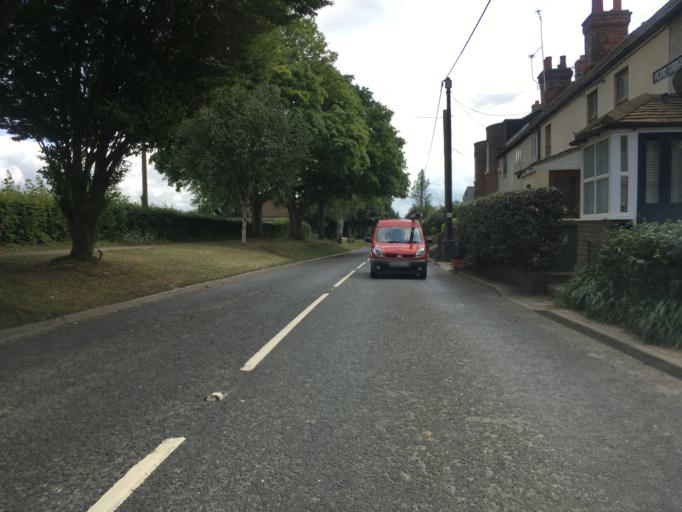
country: GB
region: England
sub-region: Kent
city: Headcorn
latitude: 51.2186
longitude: 0.5931
